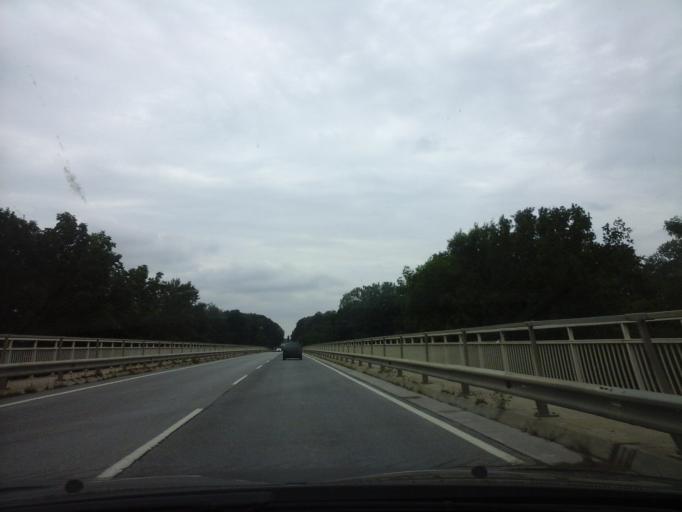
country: AT
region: Lower Austria
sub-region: Politischer Bezirk Bruck an der Leitha
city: Bad Deutsch-Altenburg
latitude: 48.1547
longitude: 16.9024
